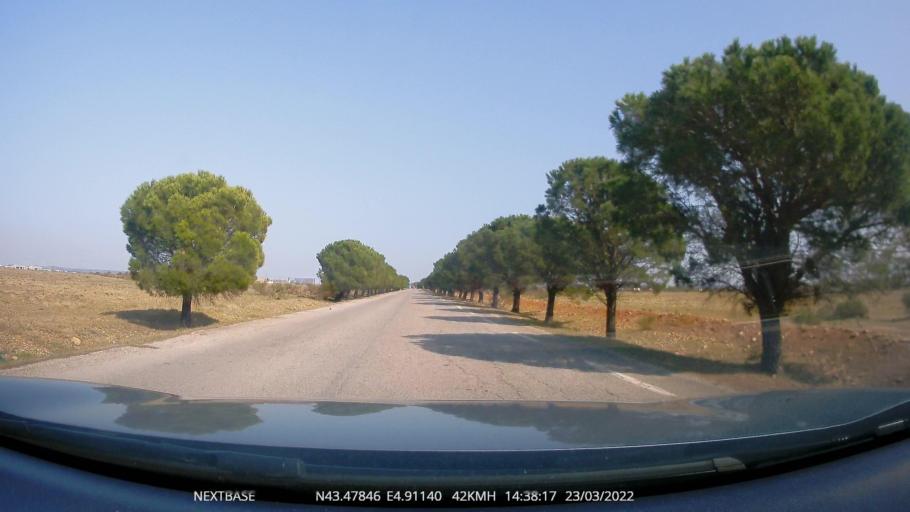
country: FR
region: Provence-Alpes-Cote d'Azur
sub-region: Departement des Bouches-du-Rhone
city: Fos-sur-Mer
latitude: 43.4785
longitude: 4.9113
